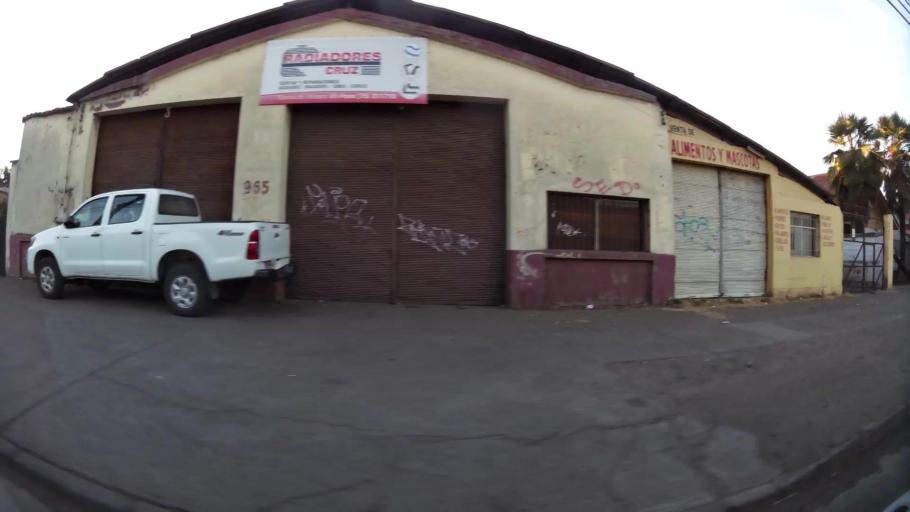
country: CL
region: Maule
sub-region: Provincia de Curico
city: Curico
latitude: -34.9796
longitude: -71.2350
